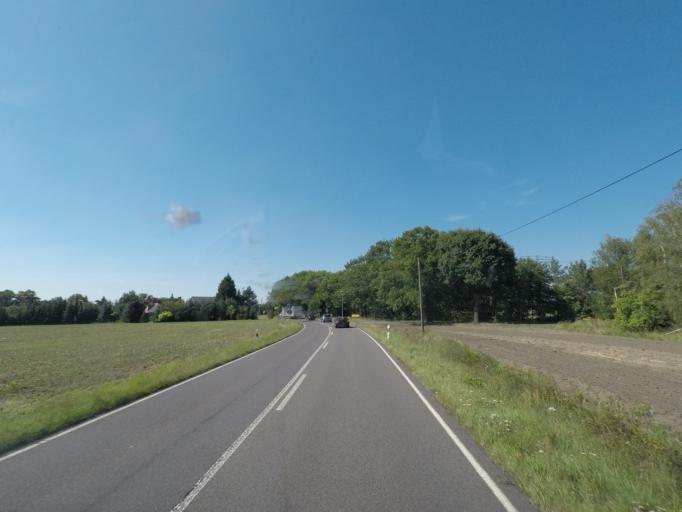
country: DE
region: Brandenburg
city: Welzow
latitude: 51.5561
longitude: 14.1388
